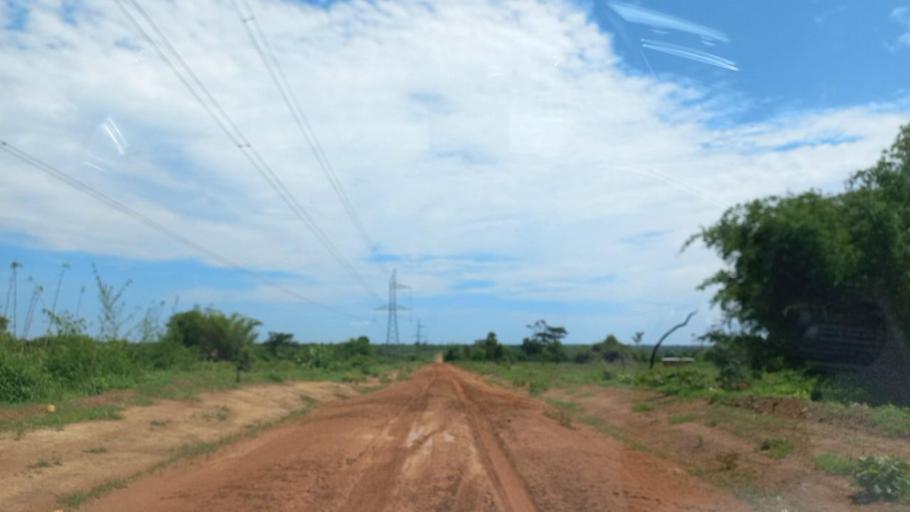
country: ZM
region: Copperbelt
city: Kitwe
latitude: -12.8367
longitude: 28.3422
